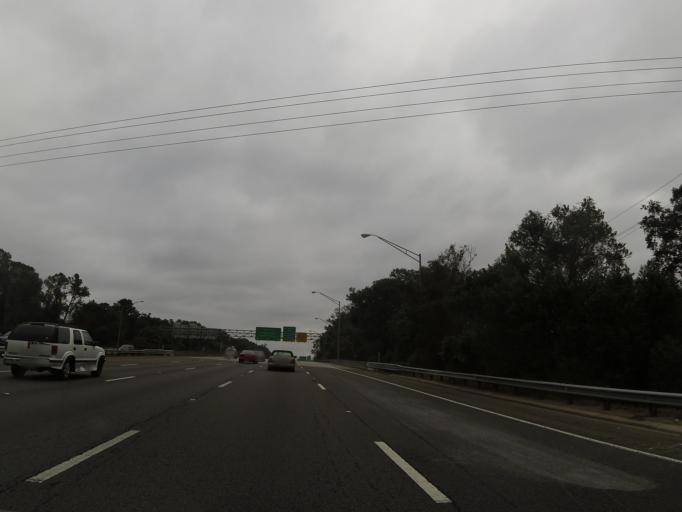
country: US
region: Florida
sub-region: Duval County
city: Jacksonville
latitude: 30.3066
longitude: -81.7705
